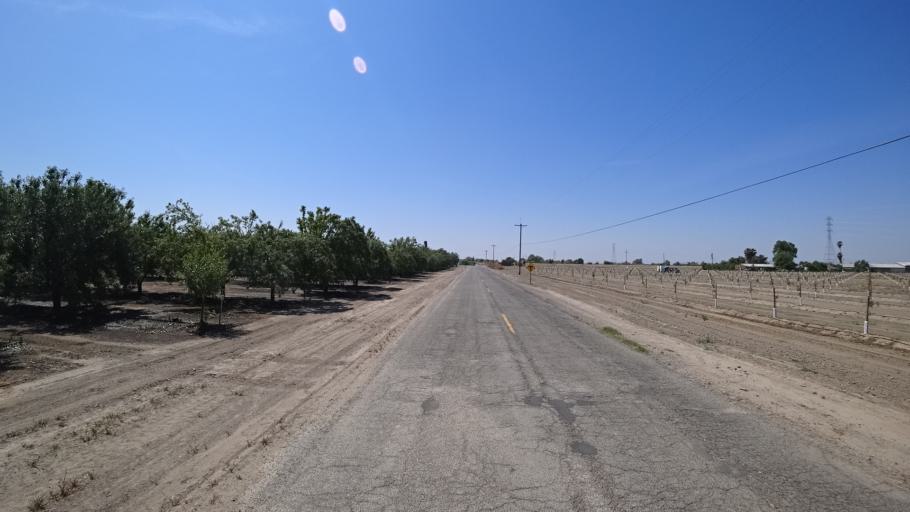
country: US
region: California
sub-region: Fresno County
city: Riverdale
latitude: 36.3894
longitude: -119.8873
